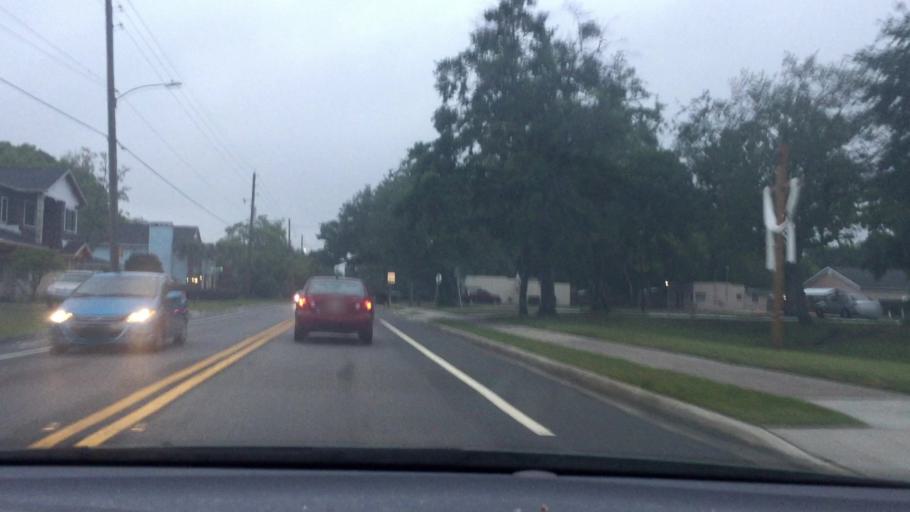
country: US
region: Florida
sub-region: Orange County
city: Fairview Shores
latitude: 28.5822
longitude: -81.3800
